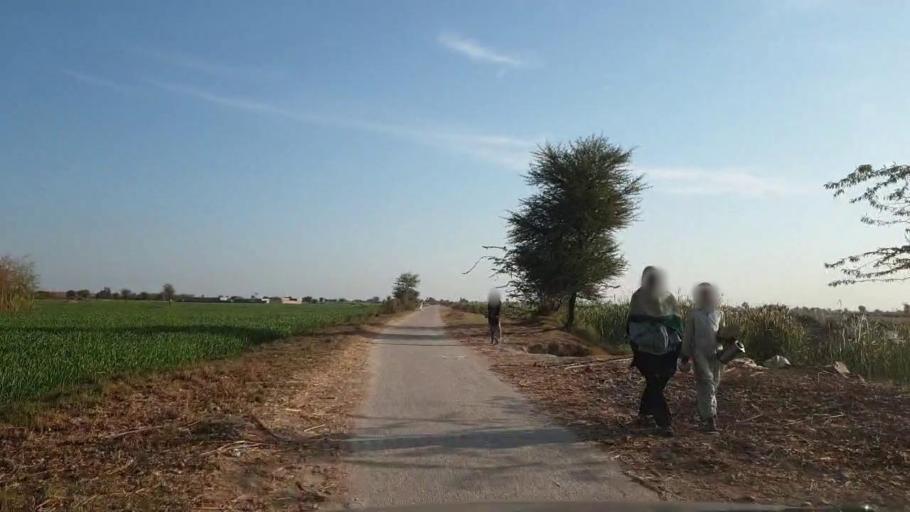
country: PK
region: Sindh
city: Khadro
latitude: 26.2107
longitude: 68.7446
